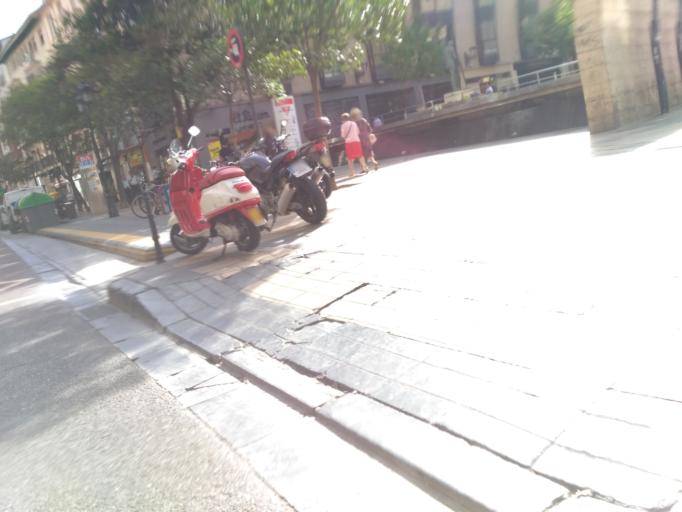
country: ES
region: Aragon
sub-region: Provincia de Zaragoza
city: Zaragoza
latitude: 41.6538
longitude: -0.8779
